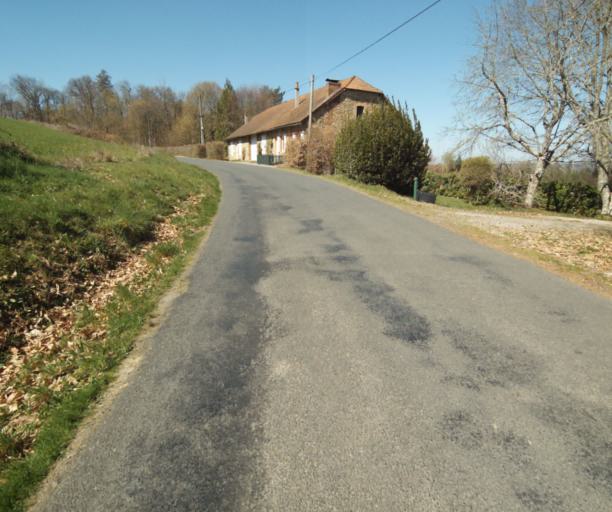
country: FR
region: Limousin
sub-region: Departement de la Correze
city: Saint-Clement
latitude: 45.2943
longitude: 1.7000
